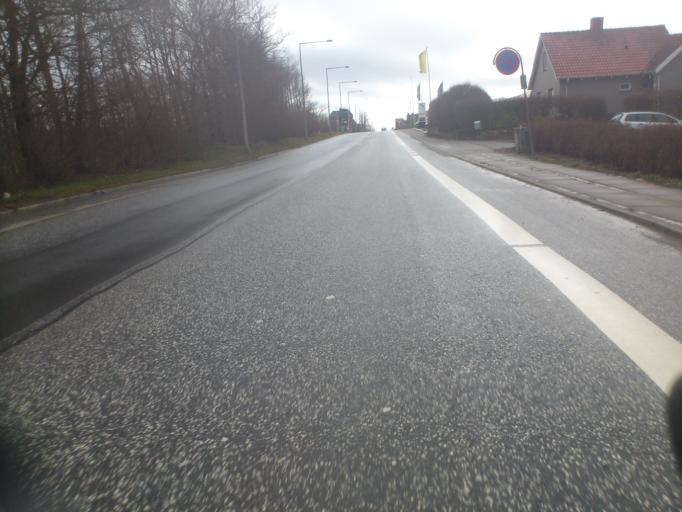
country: DK
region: South Denmark
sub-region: Fredericia Kommune
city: Fredericia
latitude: 55.5825
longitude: 9.7539
